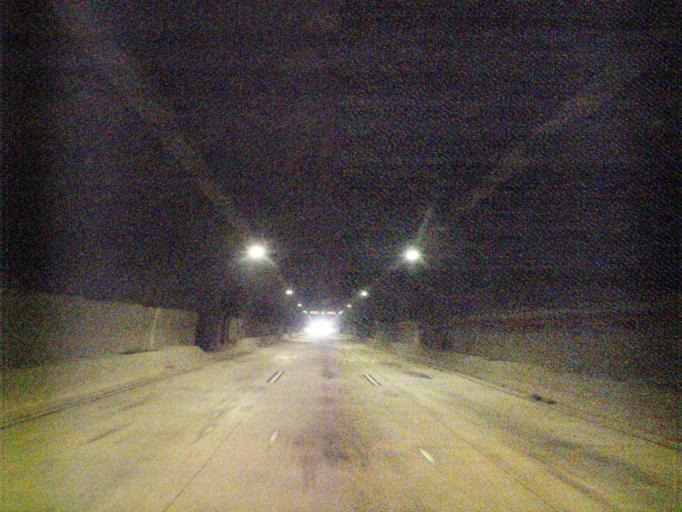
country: BR
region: Rio de Janeiro
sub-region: Rio De Janeiro
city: Rio de Janeiro
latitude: -22.8954
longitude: -43.1853
